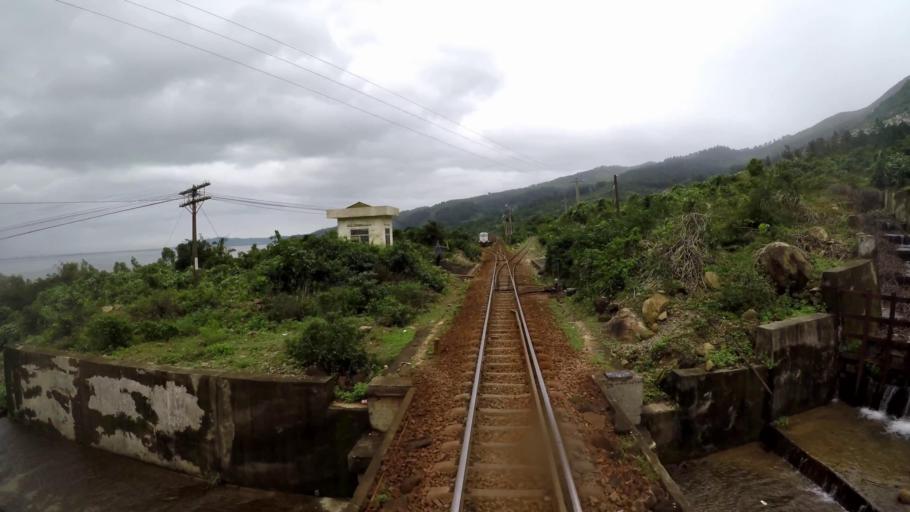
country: VN
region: Da Nang
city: Lien Chieu
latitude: 16.1686
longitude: 108.1363
